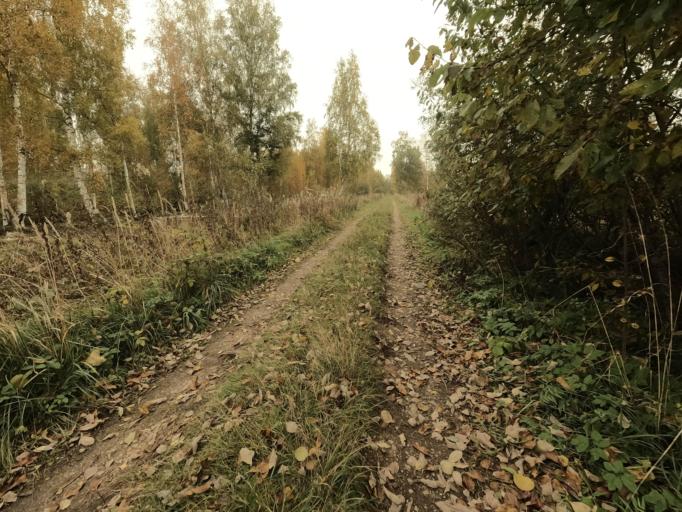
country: RU
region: Novgorod
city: Pankovka
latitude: 58.8695
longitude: 30.9359
